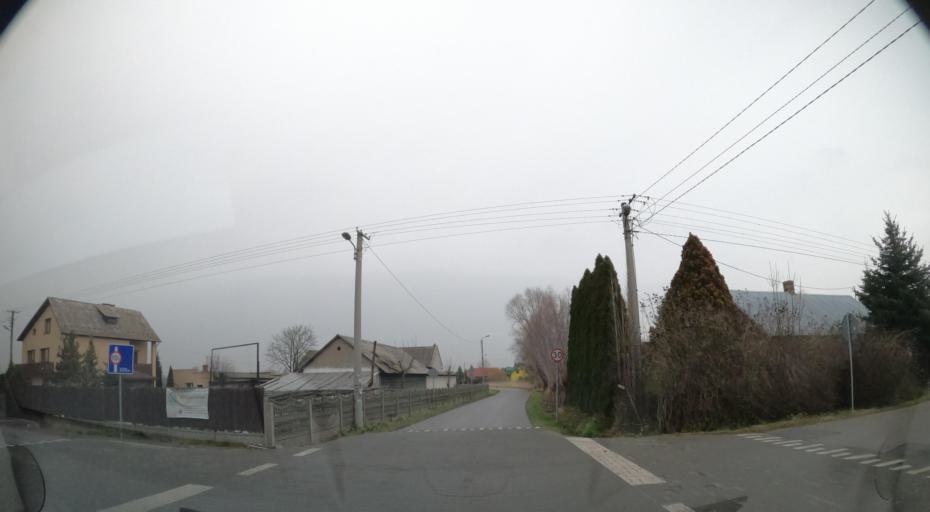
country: PL
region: Masovian Voivodeship
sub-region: Radom
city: Radom
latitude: 51.4160
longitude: 21.2228
